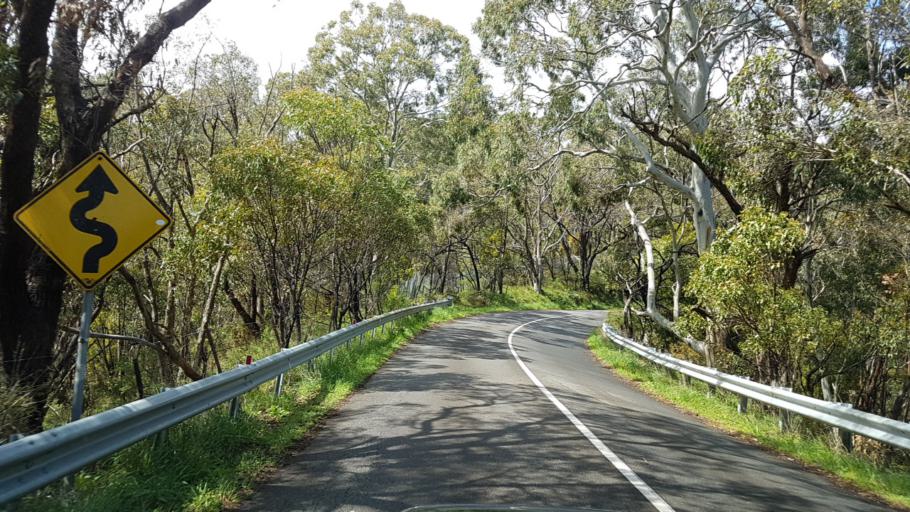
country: AU
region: South Australia
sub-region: Adelaide Hills
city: Adelaide Hills
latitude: -34.9175
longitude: 138.7562
